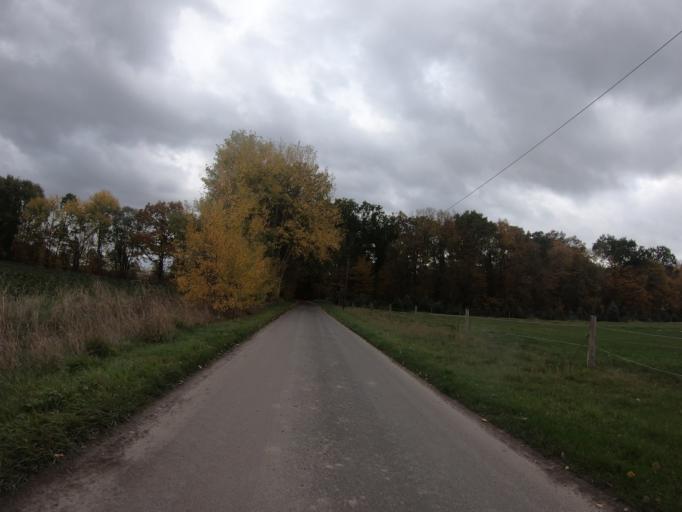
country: DE
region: Lower Saxony
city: Adenbuettel
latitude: 52.3943
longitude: 10.4817
